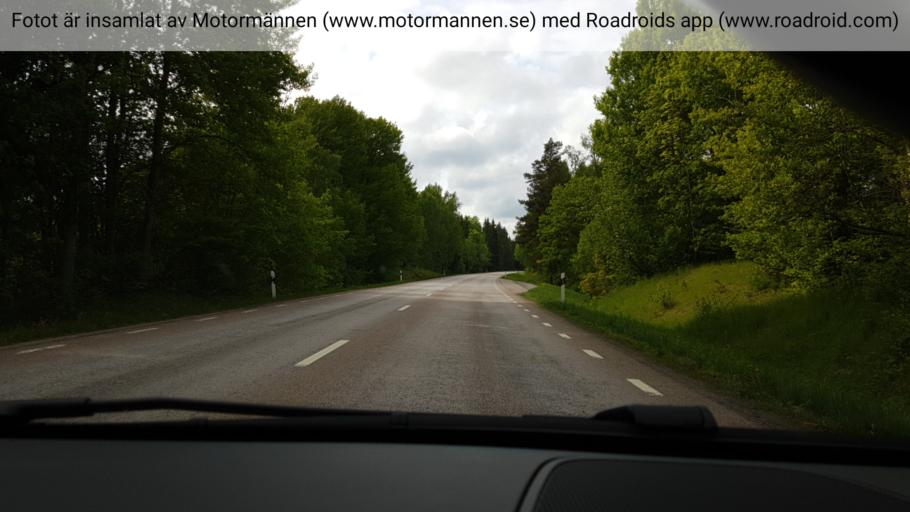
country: SE
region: Uppsala
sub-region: Osthammars Kommun
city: Osterbybruk
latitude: 60.1967
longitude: 17.8152
